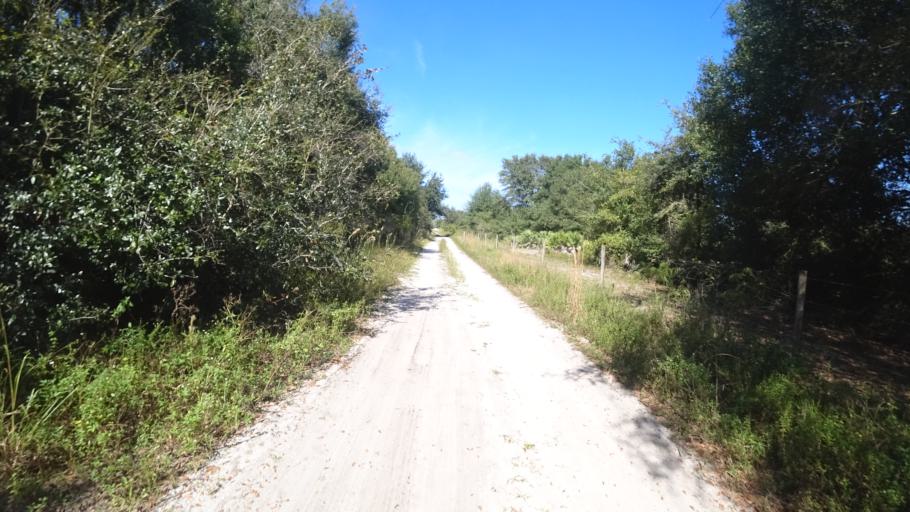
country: US
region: Florida
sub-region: DeSoto County
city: Arcadia
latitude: 27.2926
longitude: -82.0643
